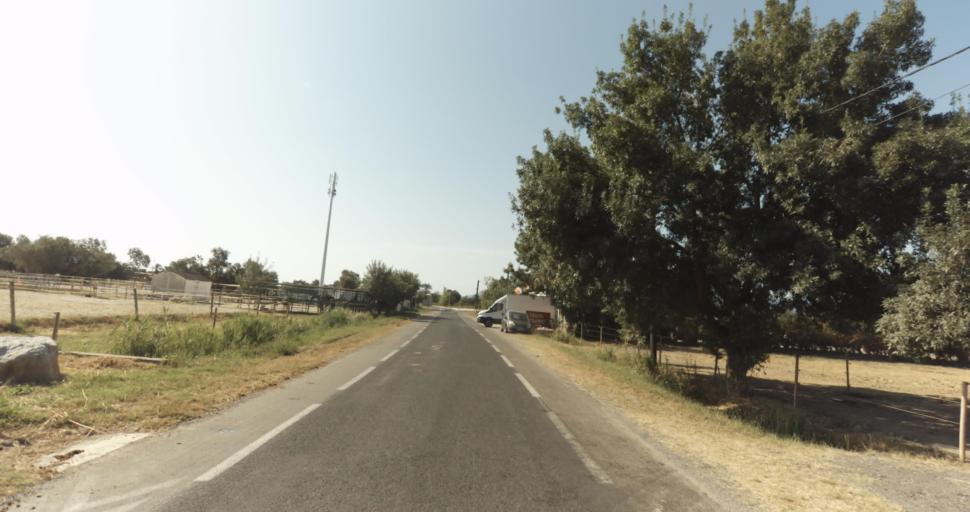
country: FR
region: Languedoc-Roussillon
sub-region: Departement des Pyrenees-Orientales
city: Saint-Cyprien-Plage
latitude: 42.6267
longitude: 3.0195
